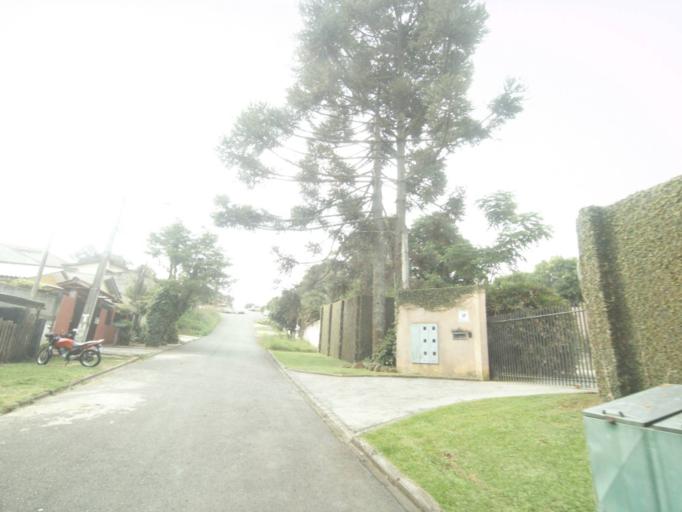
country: BR
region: Parana
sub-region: Curitiba
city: Curitiba
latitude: -25.4090
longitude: -49.3076
